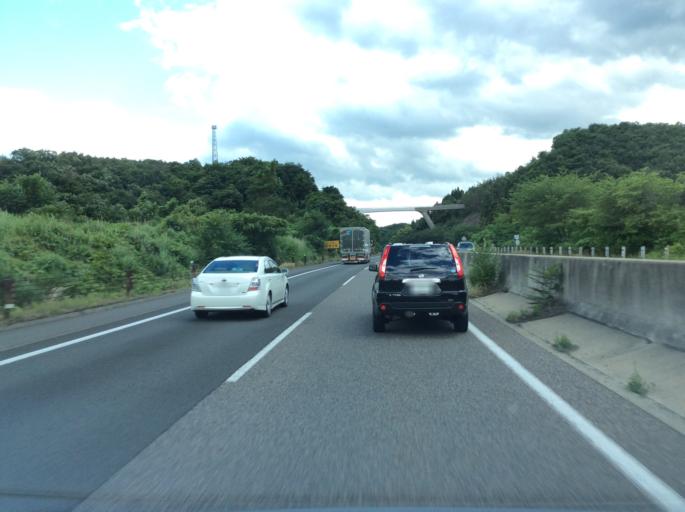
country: JP
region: Fukushima
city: Nihommatsu
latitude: 37.6399
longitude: 140.4345
